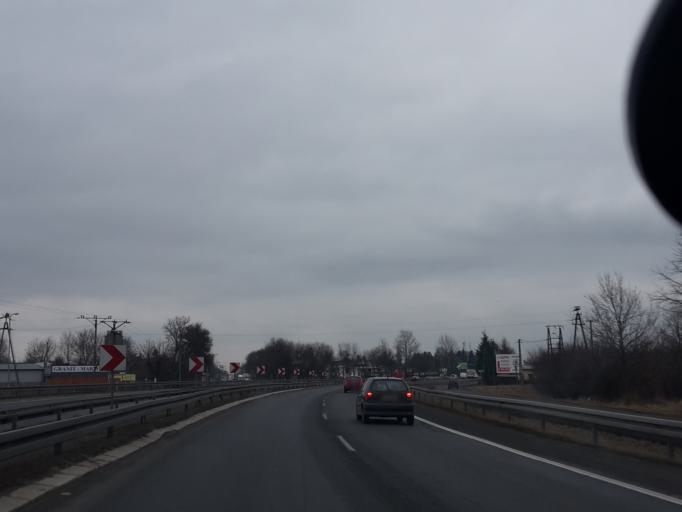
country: PL
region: Masovian Voivodeship
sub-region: Powiat warszawski zachodni
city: Dziekanow Lesny
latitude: 52.3508
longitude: 20.8563
